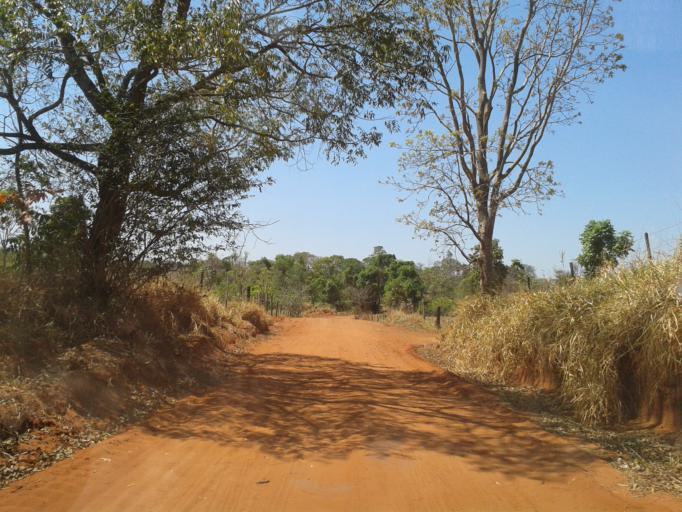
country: BR
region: Minas Gerais
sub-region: Ituiutaba
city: Ituiutaba
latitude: -19.0814
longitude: -49.3109
